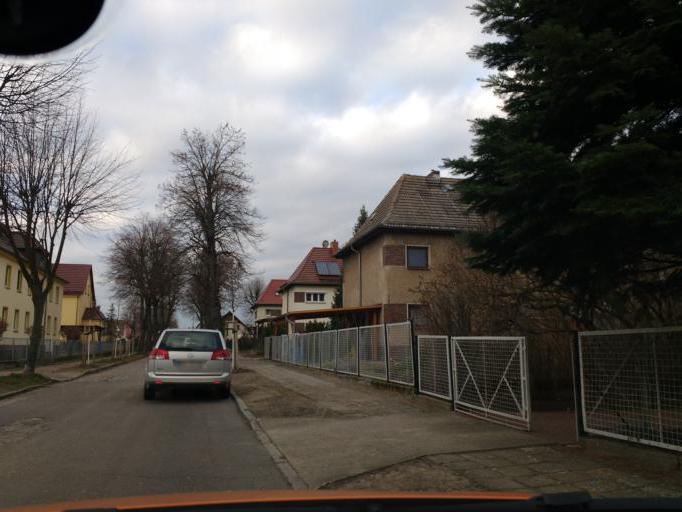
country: DE
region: Brandenburg
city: Wriezen
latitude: 52.7247
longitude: 14.1345
